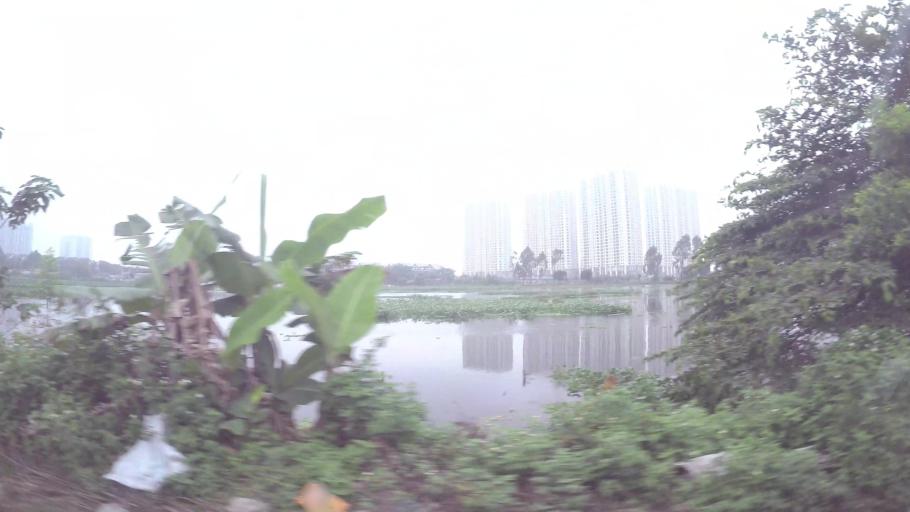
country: VN
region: Ha Noi
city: Van Dien
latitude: 20.9787
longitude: 105.8730
